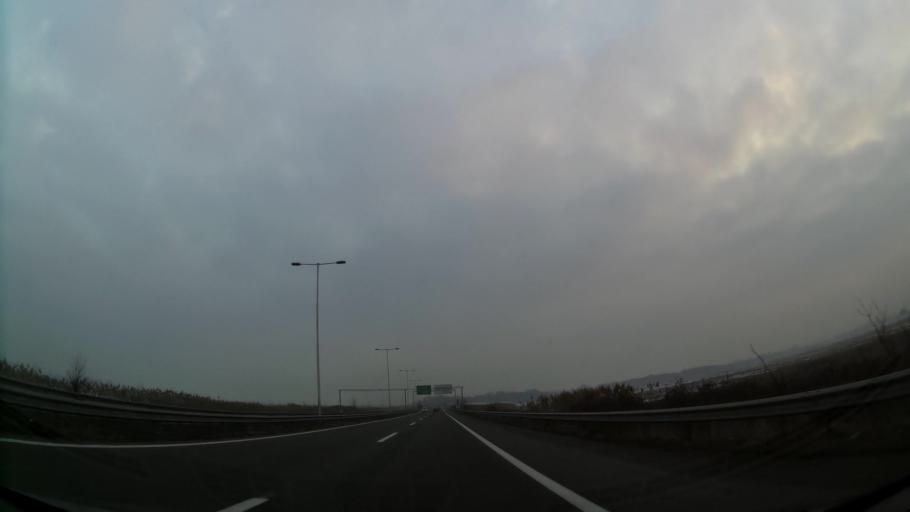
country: MK
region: Aracinovo
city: Arachinovo
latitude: 42.0017
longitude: 21.5337
